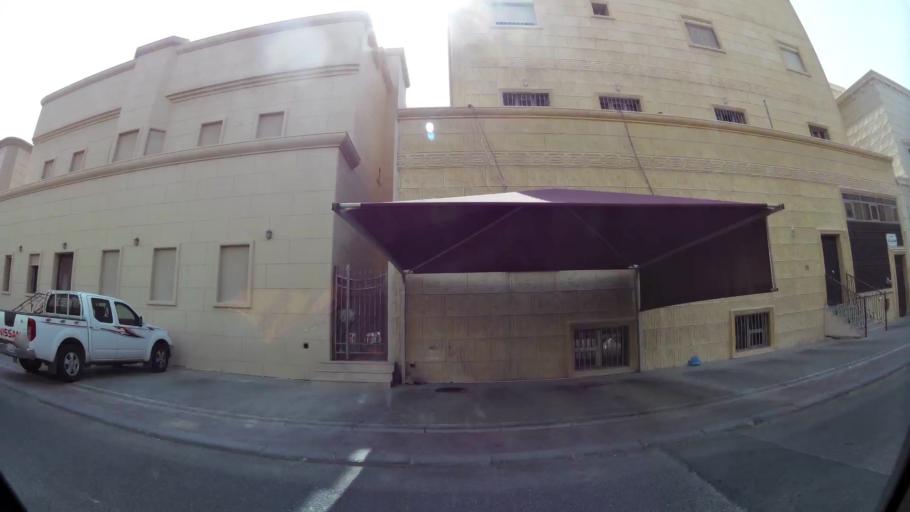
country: KW
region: Muhafazat al Jahra'
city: Al Jahra'
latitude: 29.3039
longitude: 47.6972
